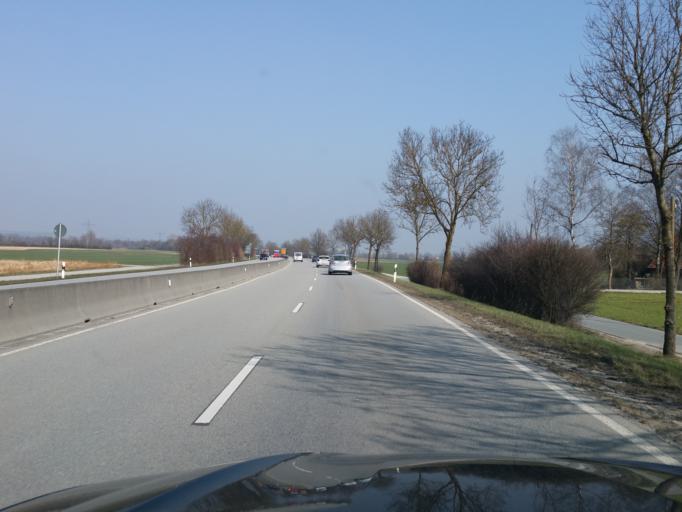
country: DE
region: Bavaria
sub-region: Lower Bavaria
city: Ergolding
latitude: 48.5666
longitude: 12.1806
